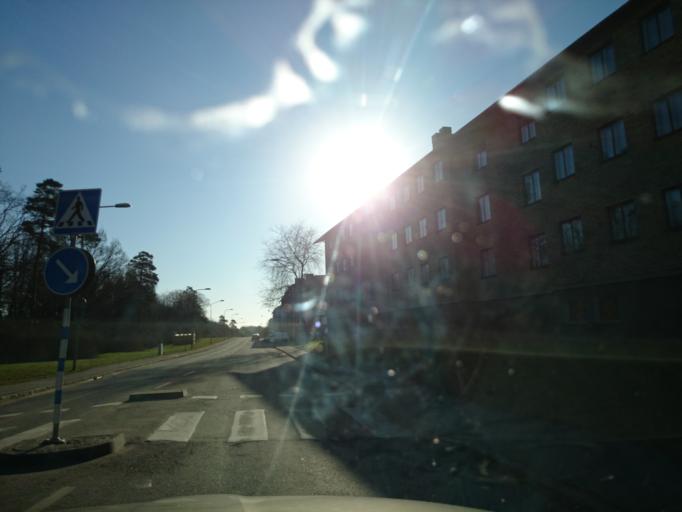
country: SE
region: Stockholm
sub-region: Huddinge Kommun
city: Segeltorp
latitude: 59.2887
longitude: 17.9659
